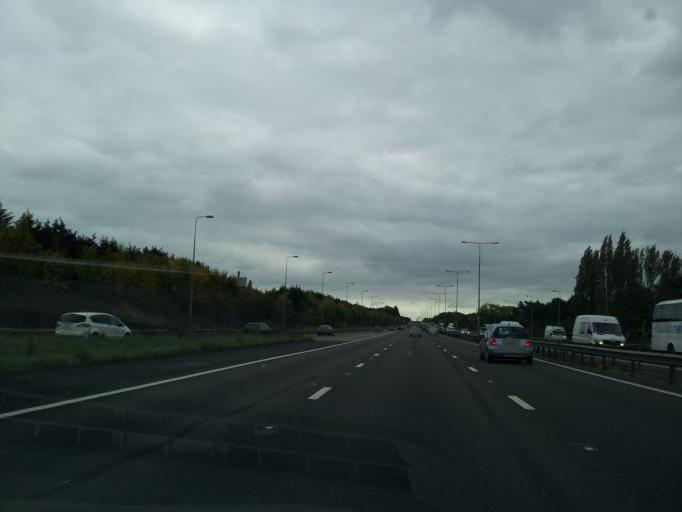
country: GB
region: England
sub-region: Northamptonshire
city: Roade
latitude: 52.1847
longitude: -0.8931
